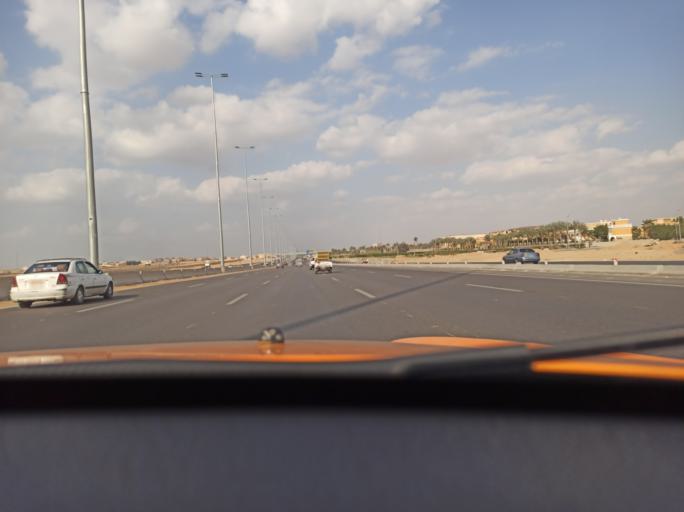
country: EG
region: Eastern Province
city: Bilbays
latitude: 30.2126
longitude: 31.6799
